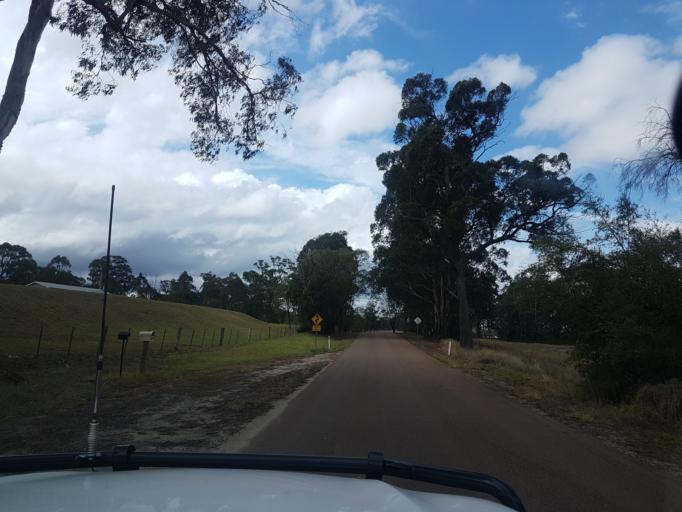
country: AU
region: Victoria
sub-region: East Gippsland
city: Bairnsdale
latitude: -37.7889
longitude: 147.5851
